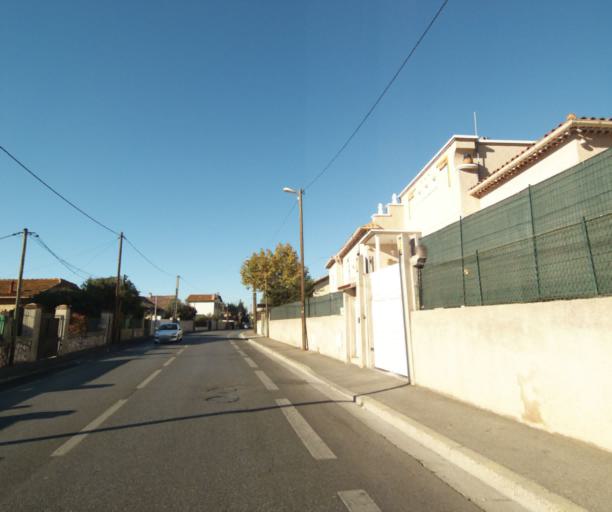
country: FR
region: Provence-Alpes-Cote d'Azur
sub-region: Departement des Bouches-du-Rhone
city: Marseille 11
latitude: 43.2892
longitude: 5.4353
